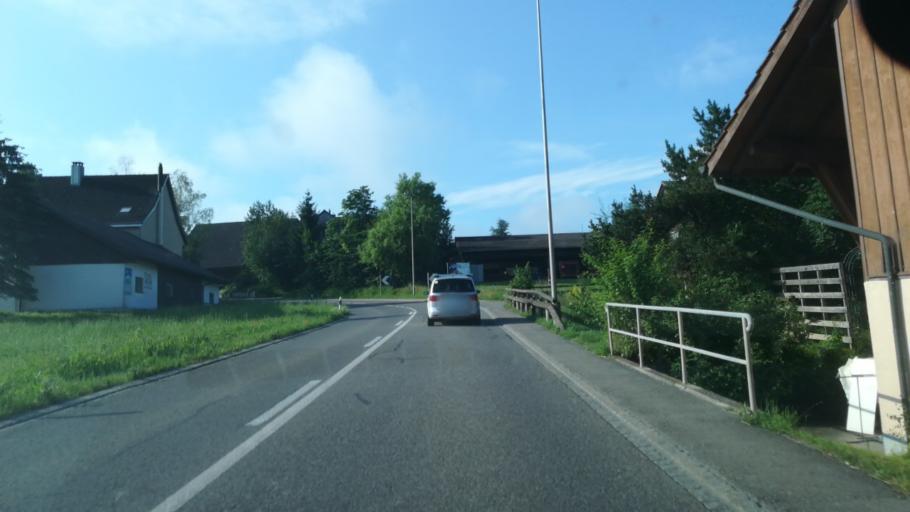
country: CH
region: Thurgau
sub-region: Weinfelden District
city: Sulgen
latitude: 47.5496
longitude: 9.1775
